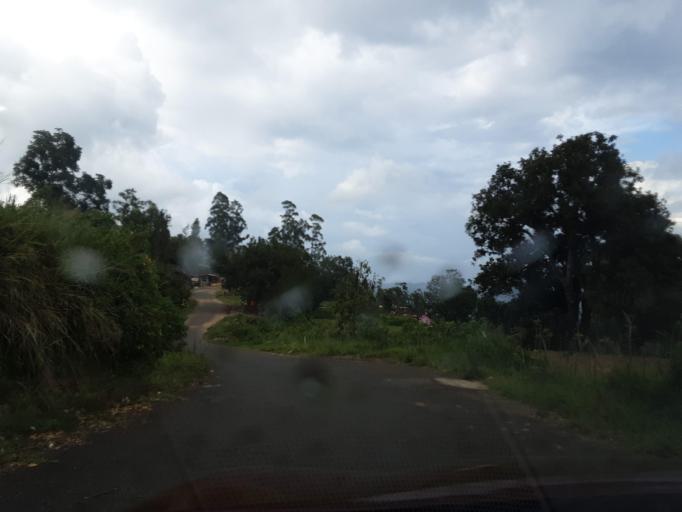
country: LK
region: Uva
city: Haputale
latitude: 6.8166
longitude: 80.8839
